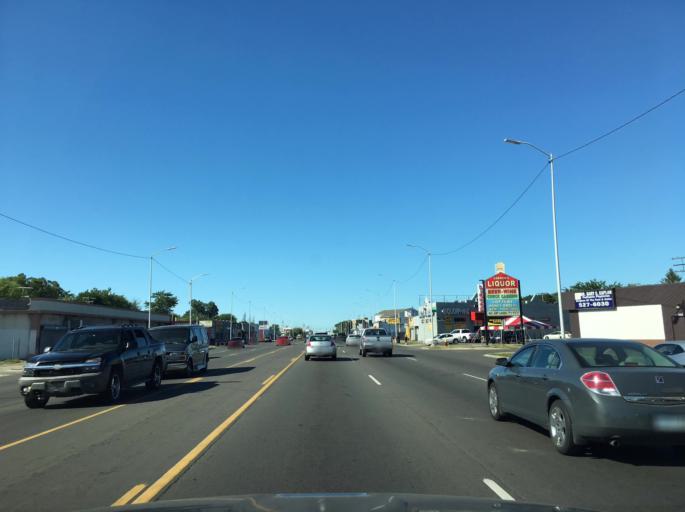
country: US
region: Michigan
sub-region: Macomb County
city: Eastpointe
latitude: 42.4388
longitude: -82.9752
